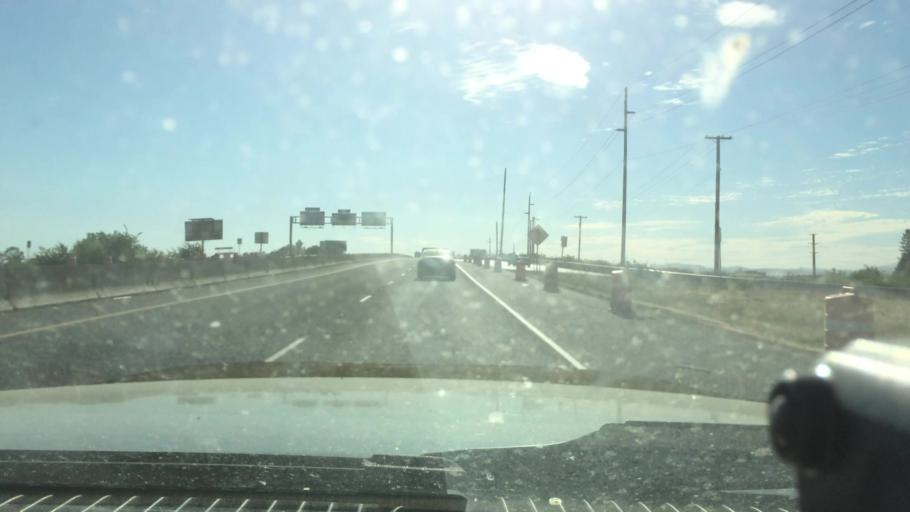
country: US
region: Oregon
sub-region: Lane County
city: Eugene
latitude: 44.0980
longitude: -123.1525
